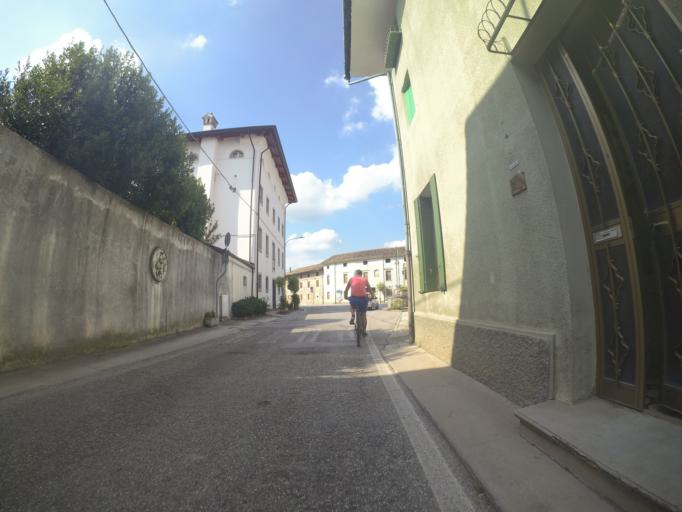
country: IT
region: Friuli Venezia Giulia
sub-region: Provincia di Udine
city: Basiliano-Vissandone
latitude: 46.0566
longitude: 13.0854
